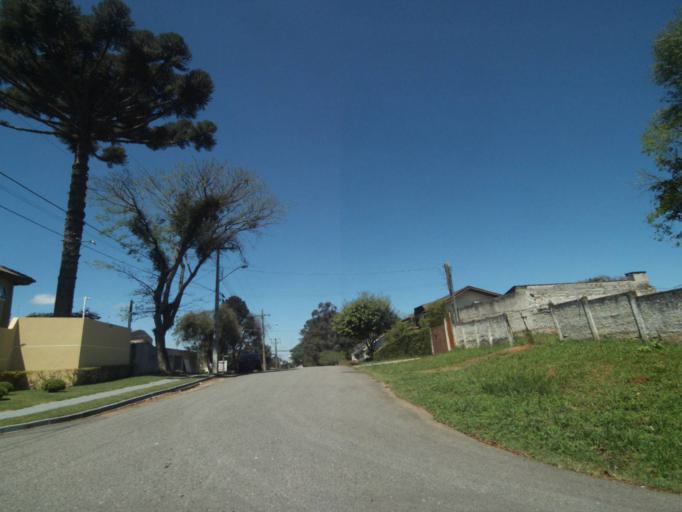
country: BR
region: Parana
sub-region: Curitiba
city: Curitiba
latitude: -25.3881
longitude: -49.2650
